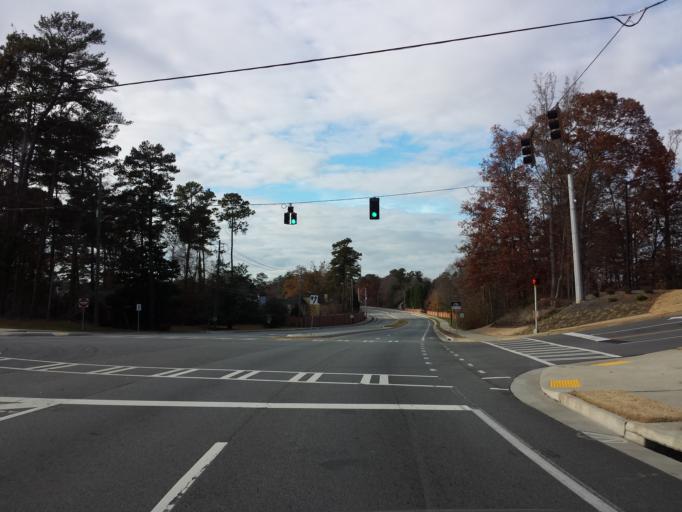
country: US
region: Georgia
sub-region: Fulton County
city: Sandy Springs
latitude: 33.9358
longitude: -84.3921
